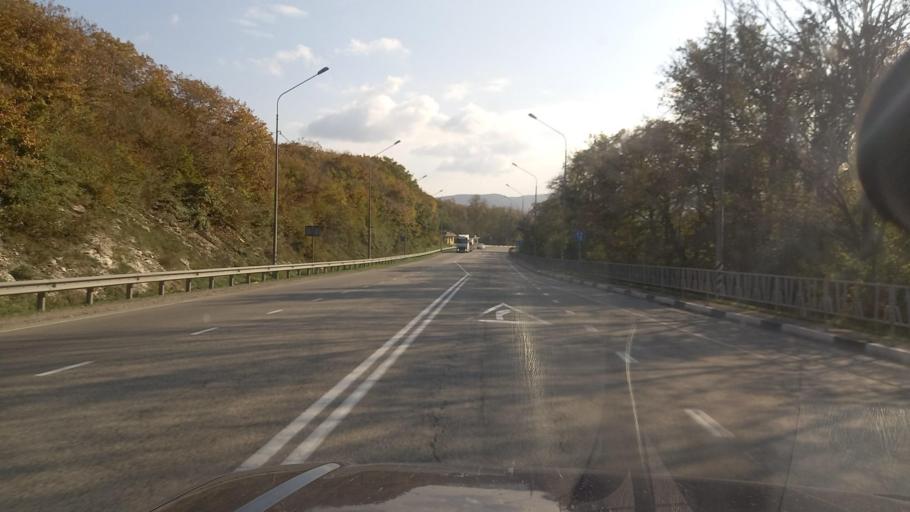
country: RU
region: Krasnodarskiy
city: Verkhnebakanskiy
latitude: 44.8456
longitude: 37.6829
